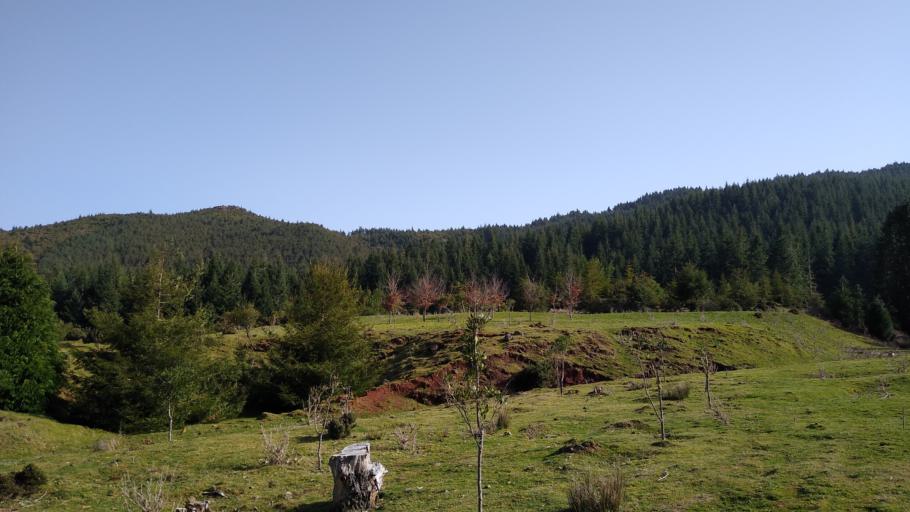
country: PT
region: Madeira
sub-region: Funchal
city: Nossa Senhora do Monte
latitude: 32.7242
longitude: -16.8861
